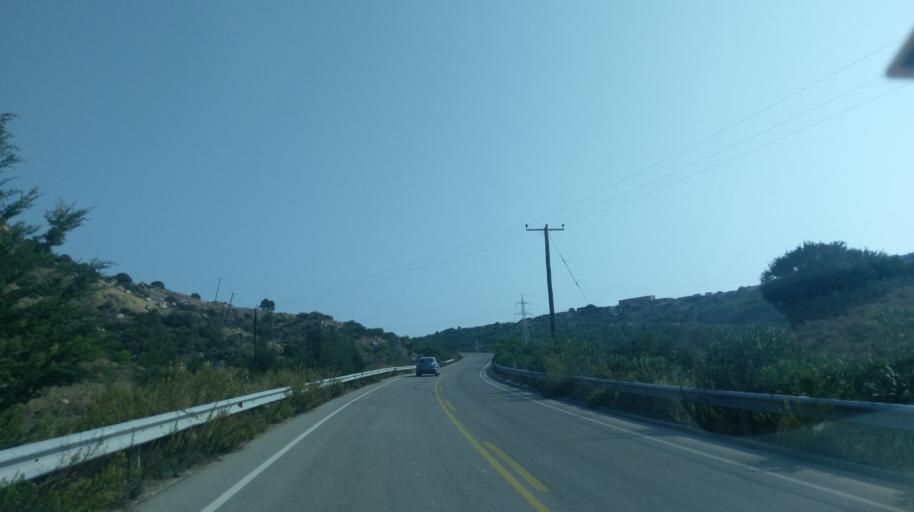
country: CY
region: Ammochostos
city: Leonarisso
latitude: 35.4774
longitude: 34.1342
